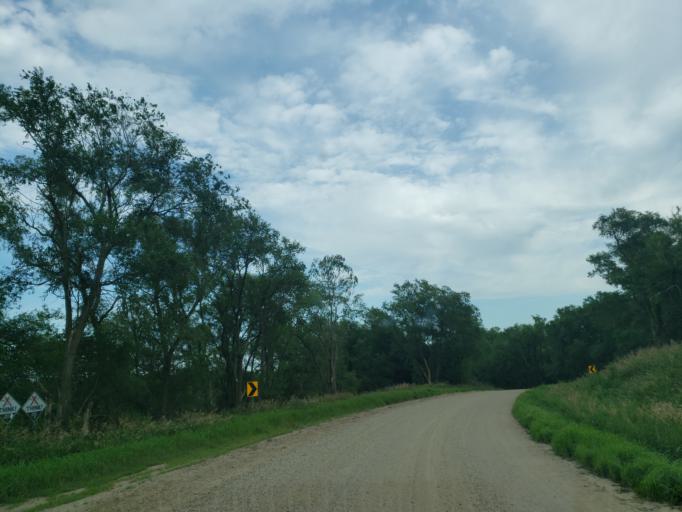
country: US
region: South Dakota
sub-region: Davison County
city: Mitchell
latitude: 43.6879
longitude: -97.9809
